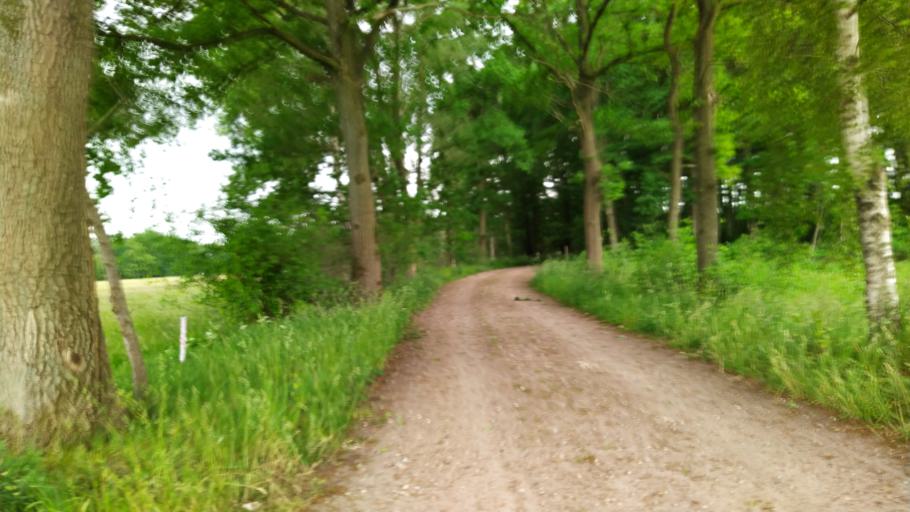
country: DE
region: Lower Saxony
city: Farven
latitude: 53.4320
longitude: 9.2767
